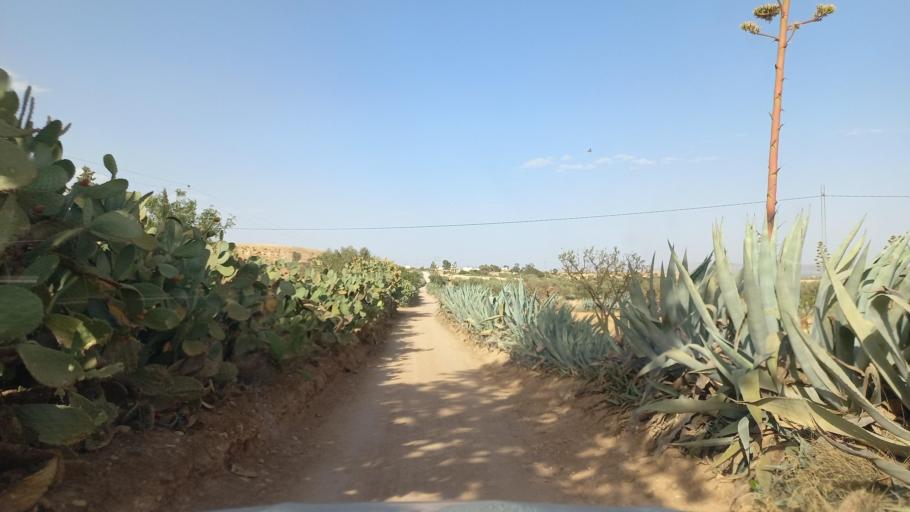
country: TN
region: Al Qasrayn
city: Kasserine
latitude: 35.2519
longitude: 8.9299
